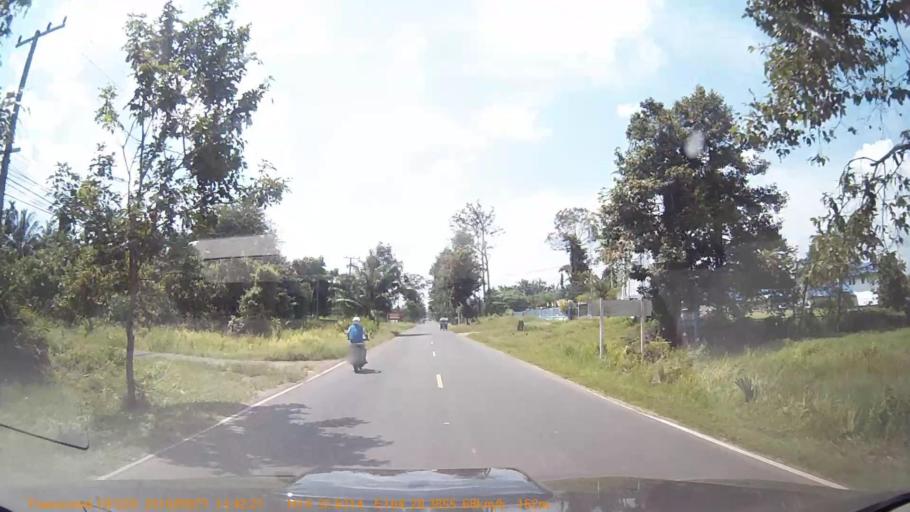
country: TH
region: Sisaket
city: Khun Han
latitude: 14.5440
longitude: 104.4728
